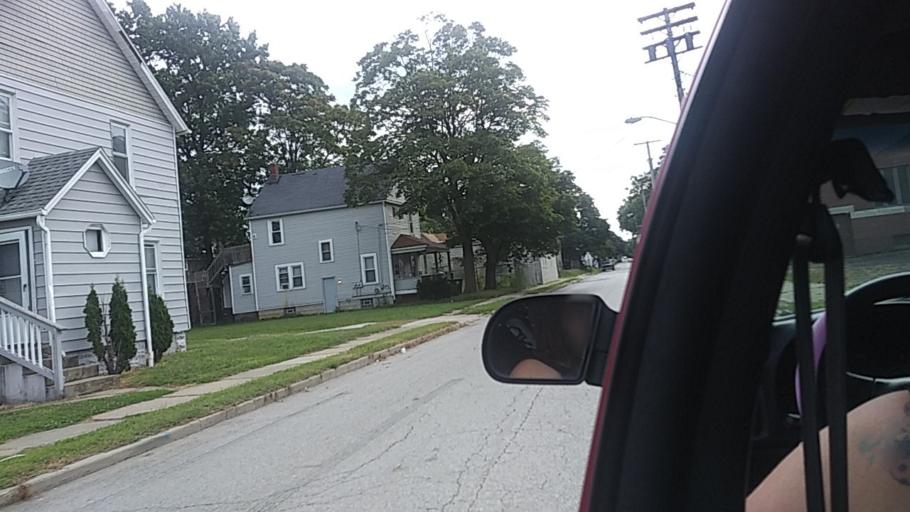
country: US
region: Ohio
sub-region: Summit County
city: Akron
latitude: 41.0637
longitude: -81.5160
